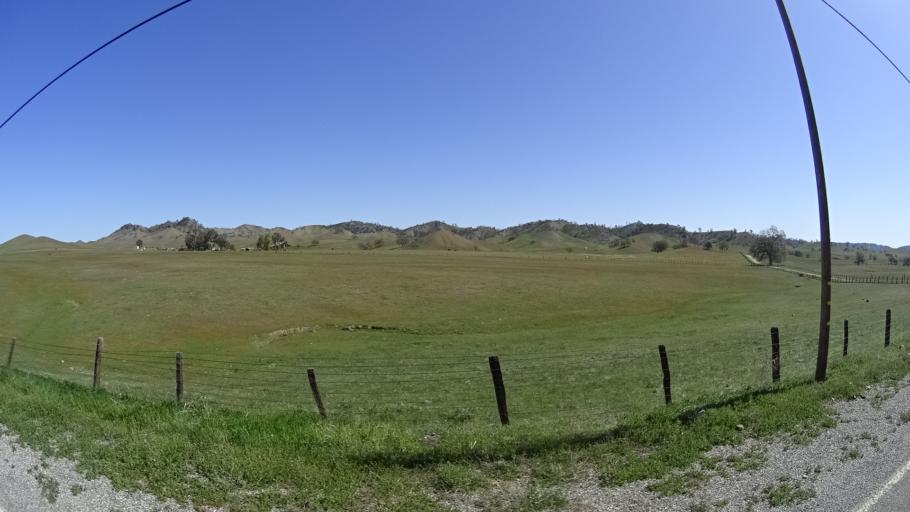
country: US
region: California
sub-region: Glenn County
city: Orland
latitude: 39.6907
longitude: -122.5466
